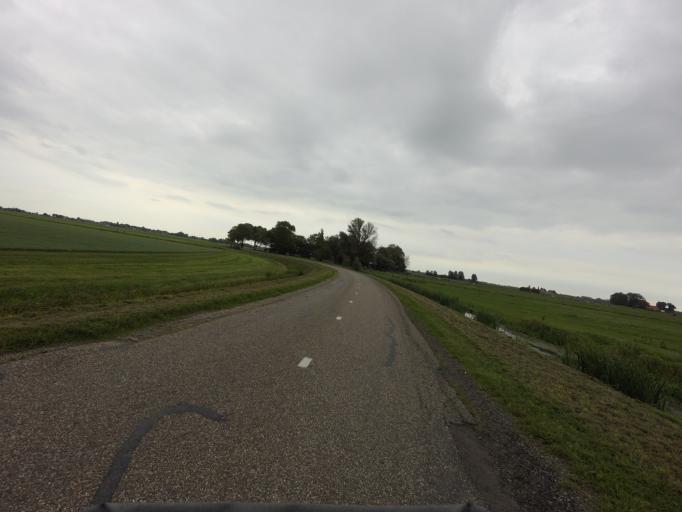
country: NL
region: Friesland
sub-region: Sudwest Fryslan
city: IJlst
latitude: 53.0267
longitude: 5.5897
